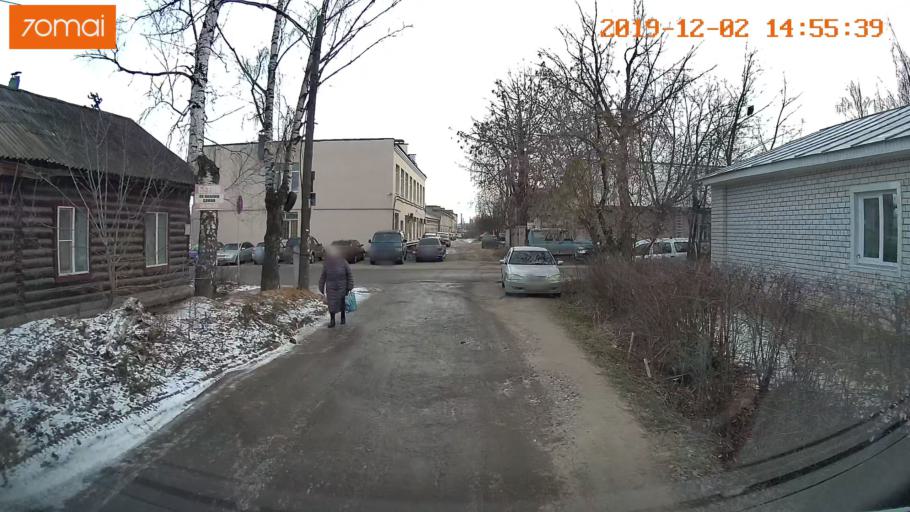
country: RU
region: Ivanovo
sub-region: Gorod Ivanovo
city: Ivanovo
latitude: 56.9727
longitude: 41.0186
